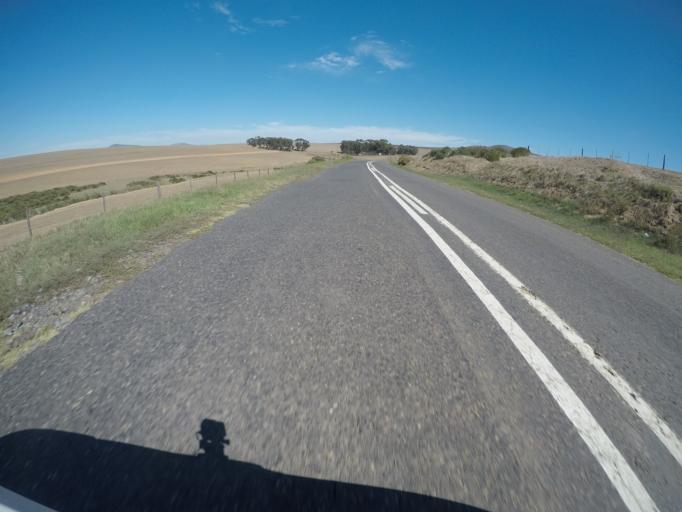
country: ZA
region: Western Cape
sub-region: City of Cape Town
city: Atlantis
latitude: -33.6953
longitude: 18.5921
